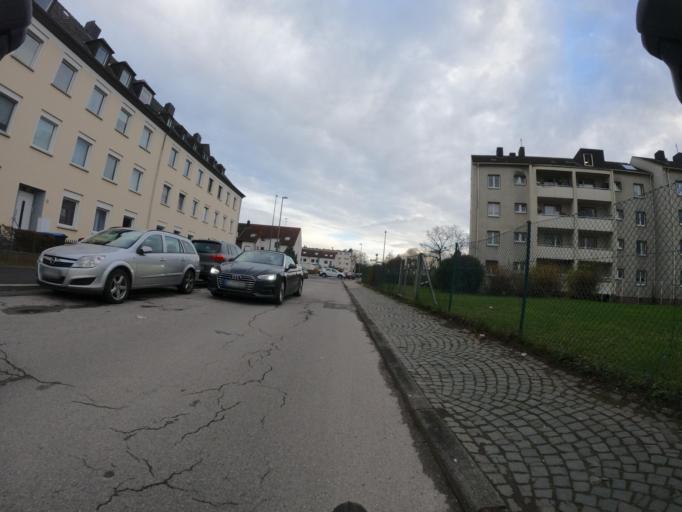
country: DE
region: North Rhine-Westphalia
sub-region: Regierungsbezirk Koln
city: Aachen
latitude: 50.7595
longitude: 6.1336
